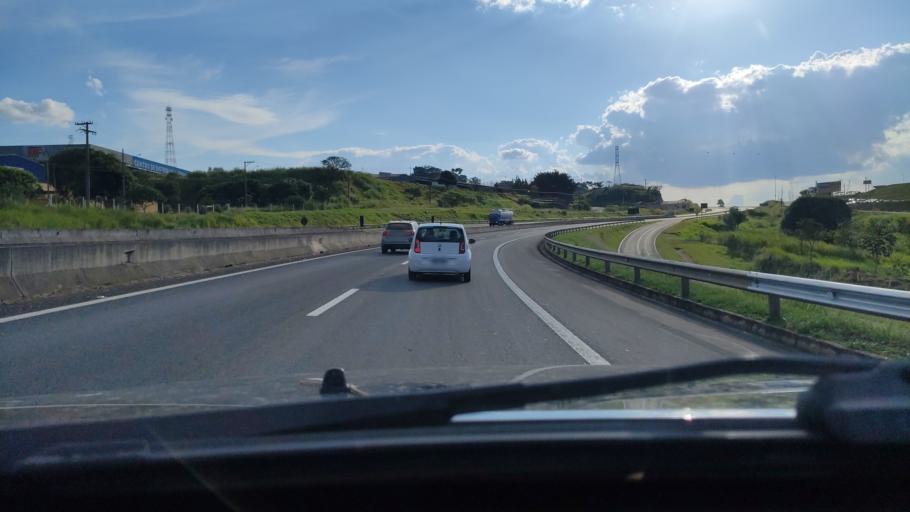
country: BR
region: Sao Paulo
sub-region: Itapira
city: Itapira
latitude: -22.4519
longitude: -46.8420
